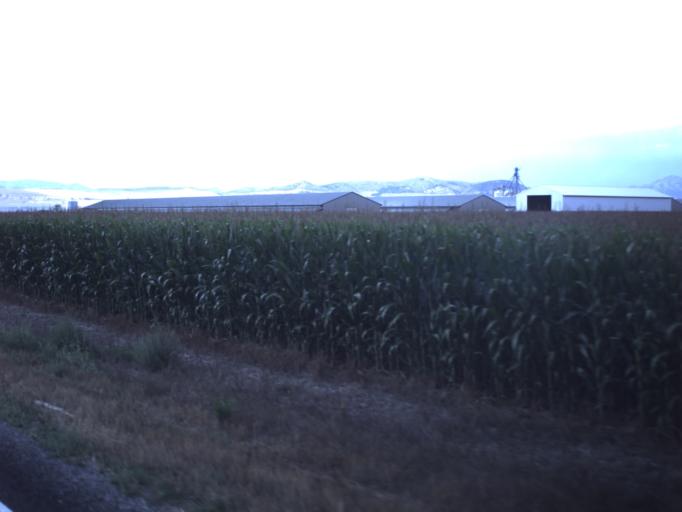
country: US
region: Utah
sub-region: Cache County
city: Lewiston
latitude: 41.9249
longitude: -111.8965
